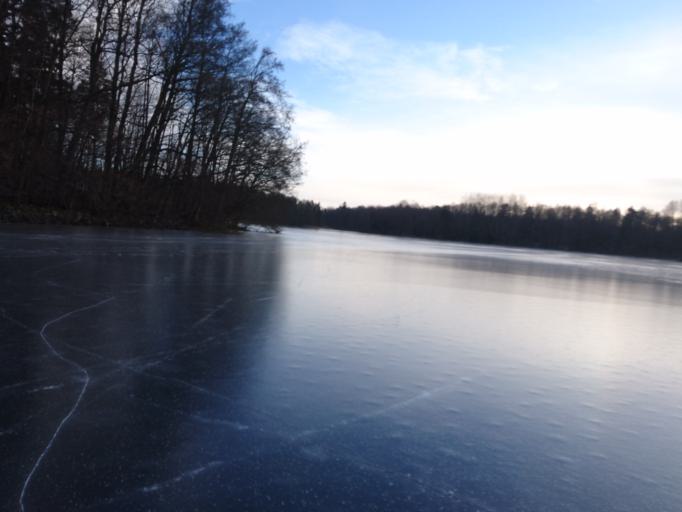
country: SE
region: Blekinge
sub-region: Karlshamns Kommun
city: Karlshamn
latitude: 56.2373
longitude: 14.9686
